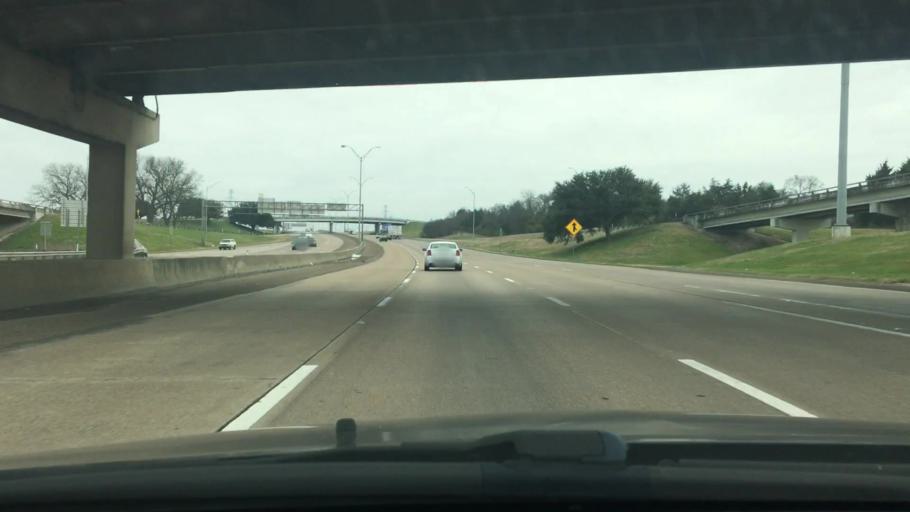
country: US
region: Texas
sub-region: Dallas County
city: Hutchins
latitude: 32.6602
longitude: -96.7248
